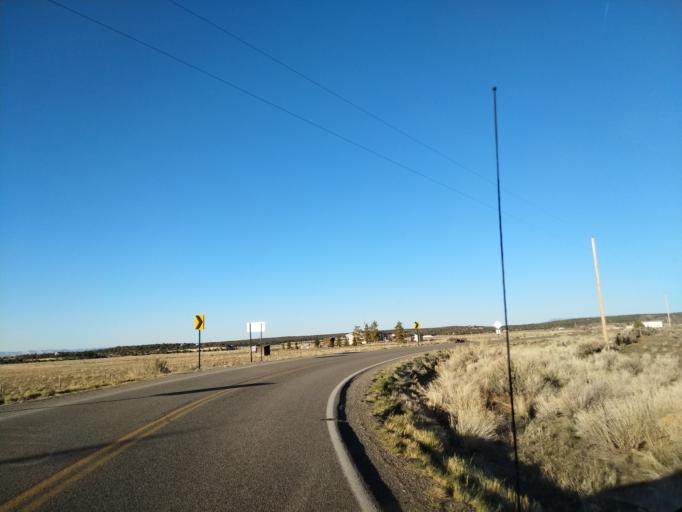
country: US
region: Colorado
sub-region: Mesa County
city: Redlands
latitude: 38.9935
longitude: -108.7506
